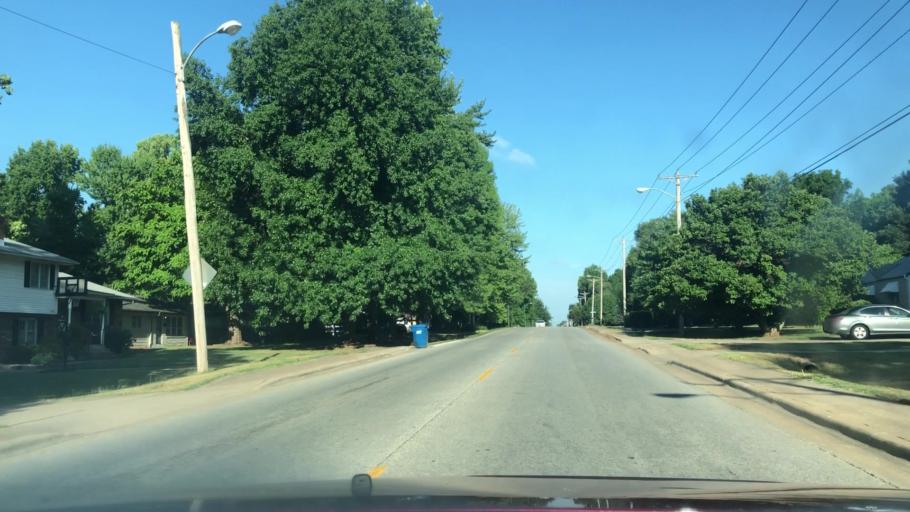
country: US
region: Missouri
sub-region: Greene County
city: Springfield
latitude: 37.1737
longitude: -93.2481
